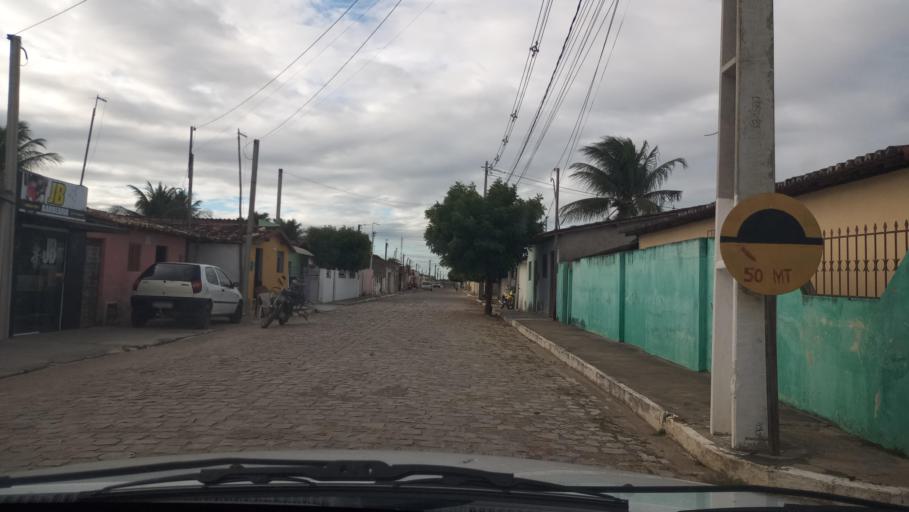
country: BR
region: Rio Grande do Norte
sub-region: Brejinho
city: Brejinho
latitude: -6.0484
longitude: -35.4334
